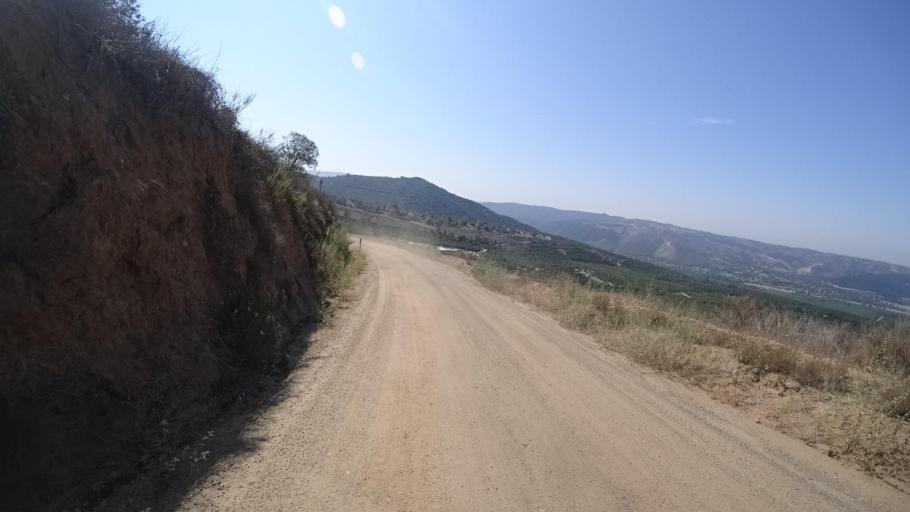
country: US
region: California
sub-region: San Diego County
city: Valley Center
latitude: 33.3264
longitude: -116.9673
